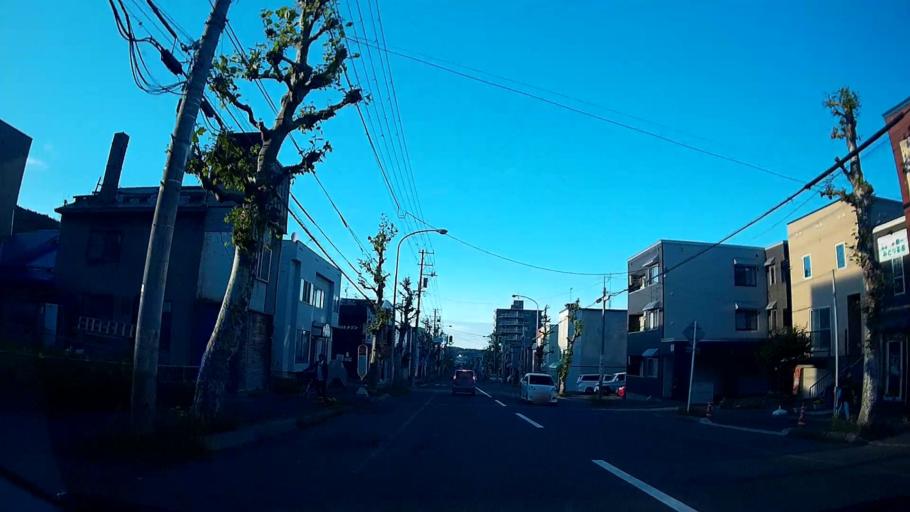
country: JP
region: Hokkaido
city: Otaru
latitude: 43.1883
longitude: 140.9892
